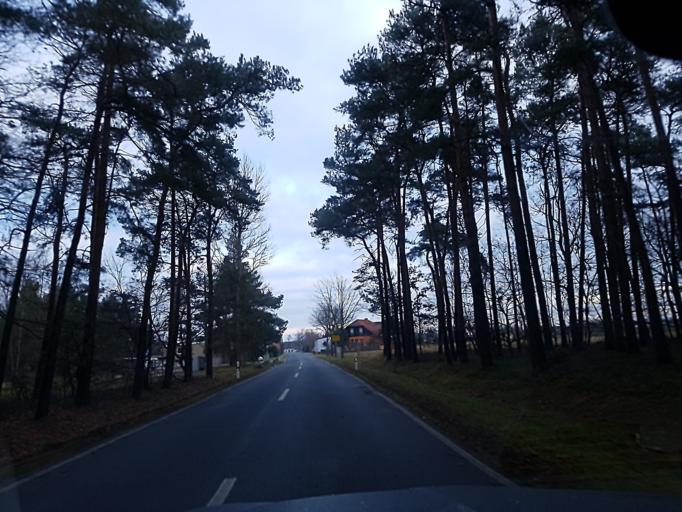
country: DE
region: Brandenburg
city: Schilda
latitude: 51.5744
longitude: 13.3557
